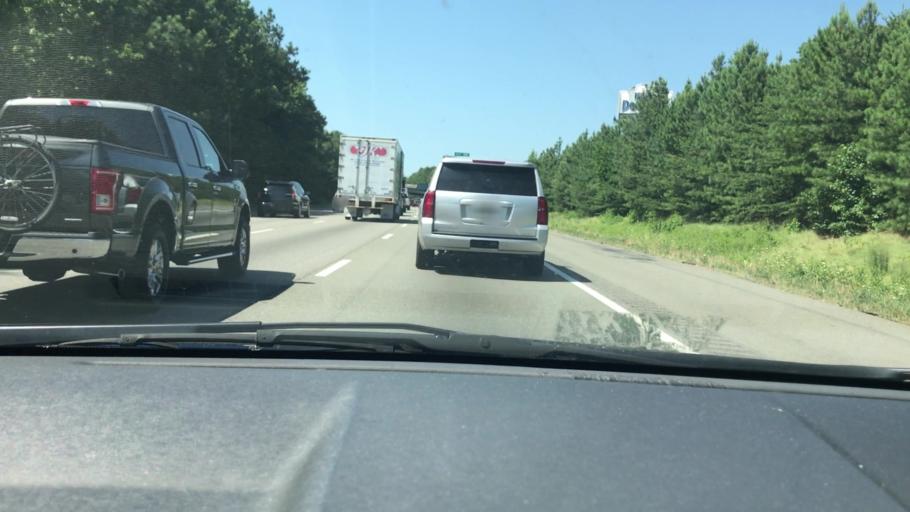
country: US
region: Virginia
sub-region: Hanover County
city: Ashland
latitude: 37.8387
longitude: -77.4506
